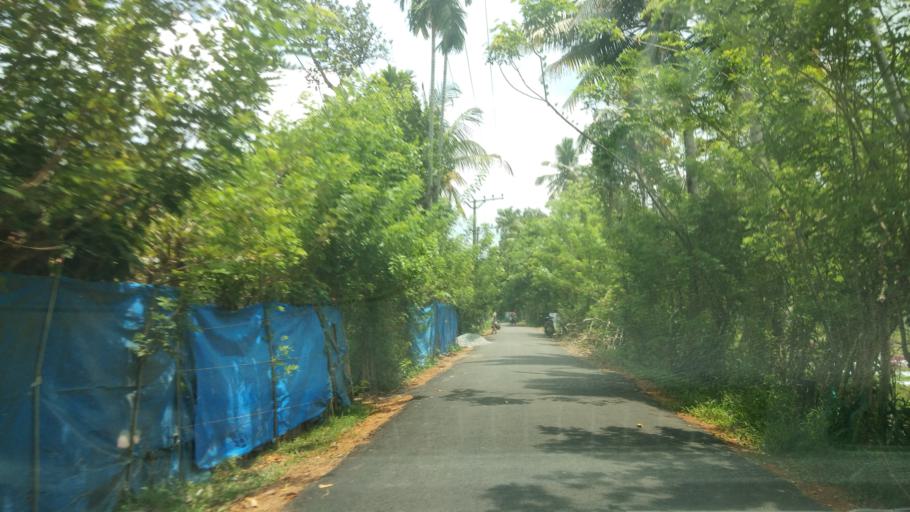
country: IN
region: Kerala
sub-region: Alappuzha
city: Shertallai
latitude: 9.6541
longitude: 76.3311
